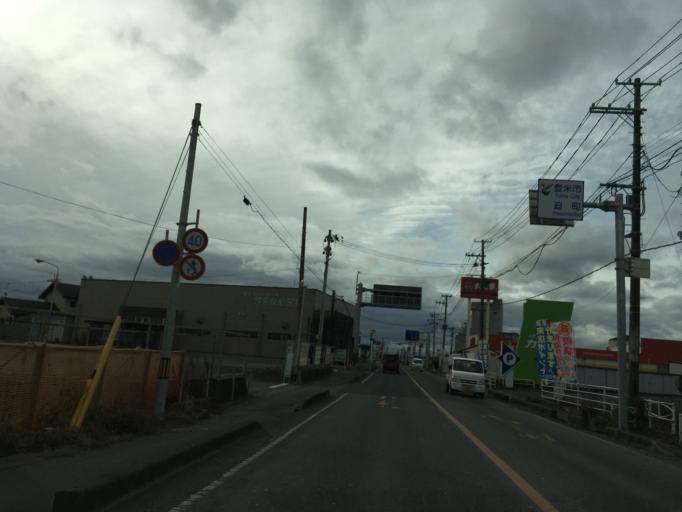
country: JP
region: Miyagi
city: Wakuya
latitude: 38.6961
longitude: 141.2112
